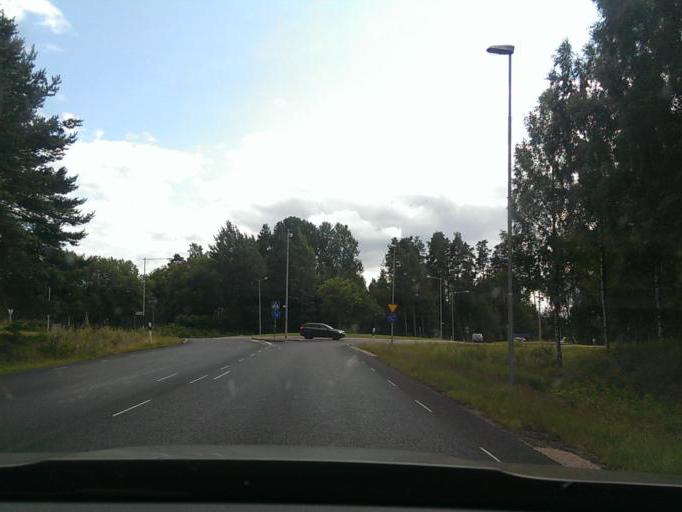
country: SE
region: Joenkoeping
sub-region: Varnamo Kommun
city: Varnamo
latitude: 57.1822
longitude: 14.0070
